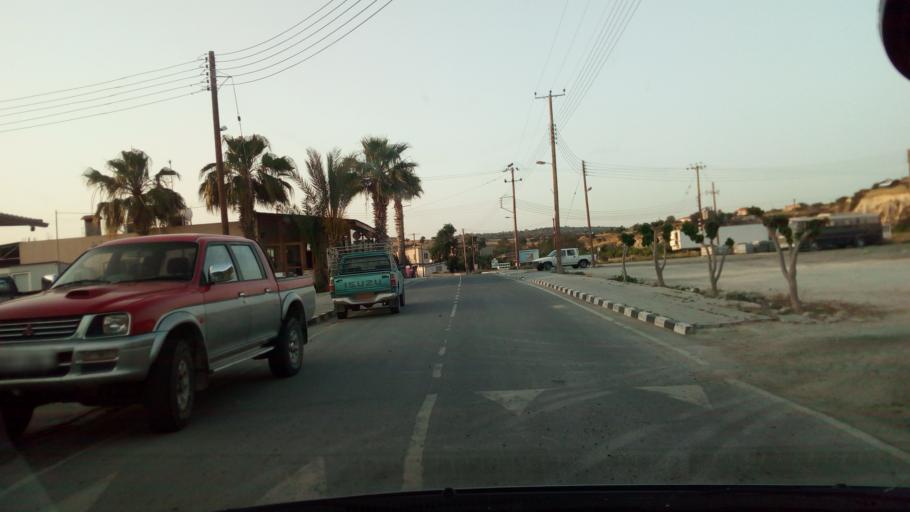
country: CY
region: Larnaka
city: Kofinou
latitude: 34.7954
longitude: 33.3850
